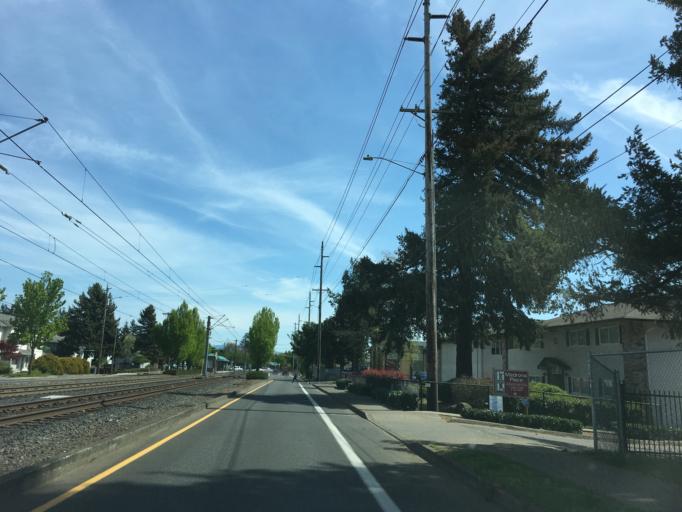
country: US
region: Oregon
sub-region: Multnomah County
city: Fairview
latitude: 45.5220
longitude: -122.4802
